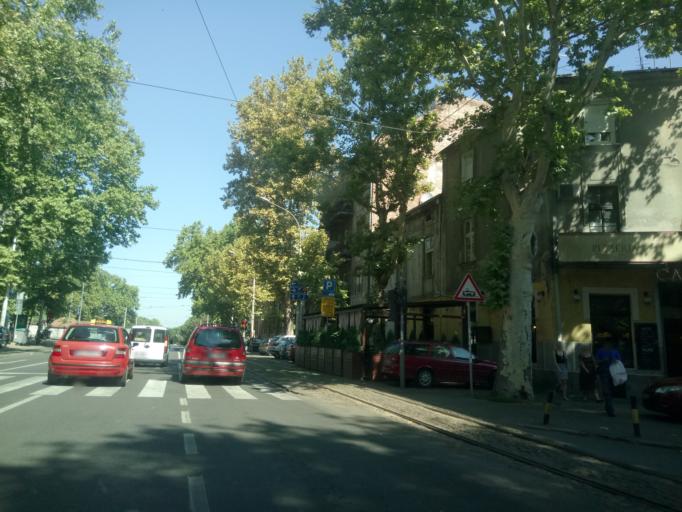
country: RS
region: Central Serbia
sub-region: Belgrade
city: Stari Grad
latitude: 44.8252
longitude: 20.4568
